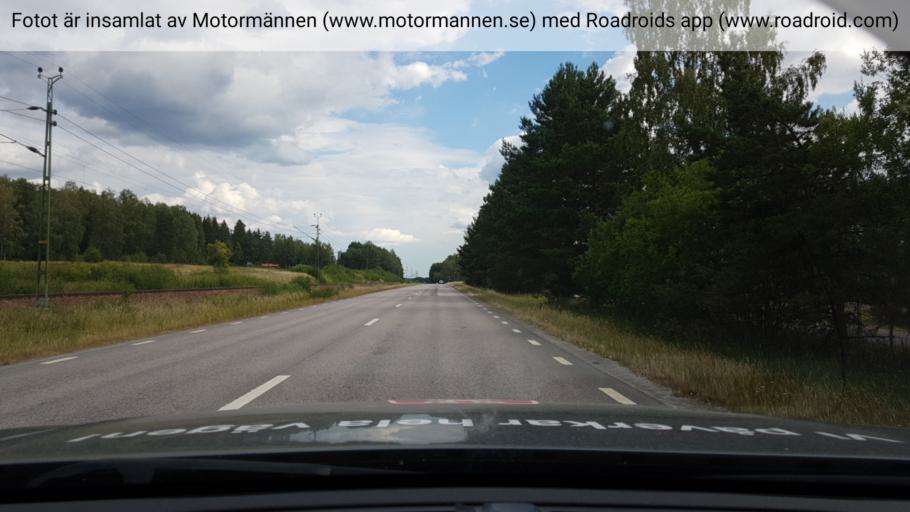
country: SE
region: Uppsala
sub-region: Heby Kommun
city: Morgongava
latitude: 59.9286
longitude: 16.9765
